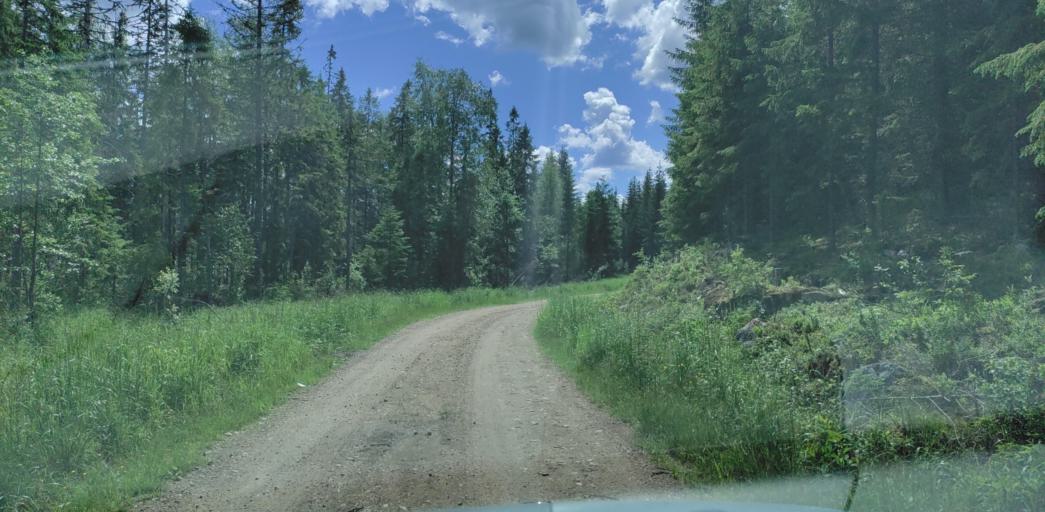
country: SE
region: Vaermland
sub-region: Hagfors Kommun
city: Ekshaerad
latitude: 60.1139
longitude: 13.3254
